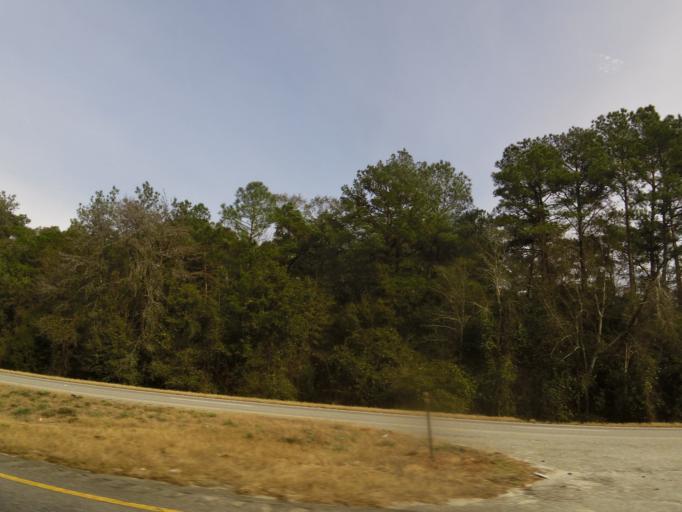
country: US
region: Alabama
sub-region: Dale County
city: Newton
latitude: 31.3469
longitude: -85.5531
